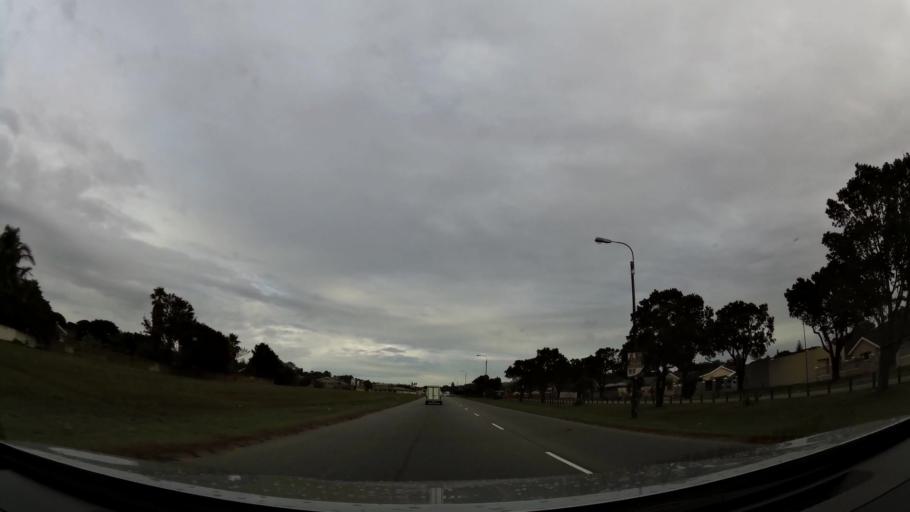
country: ZA
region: Eastern Cape
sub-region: Nelson Mandela Bay Metropolitan Municipality
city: Port Elizabeth
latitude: -33.9929
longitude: 25.5449
